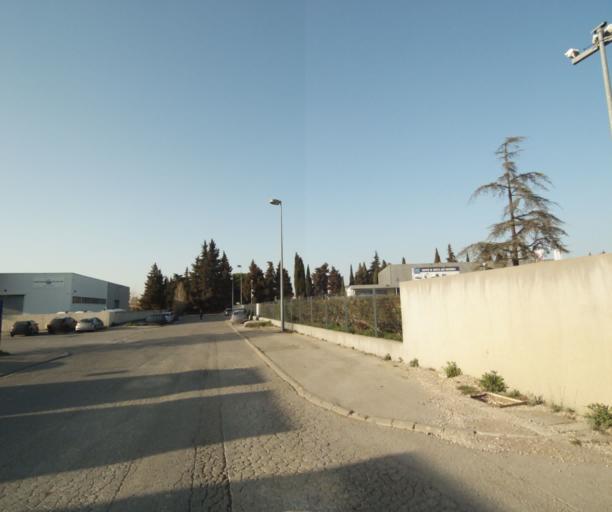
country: FR
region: Provence-Alpes-Cote d'Azur
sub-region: Departement des Bouches-du-Rhone
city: Saint-Victoret
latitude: 43.4254
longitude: 5.2579
